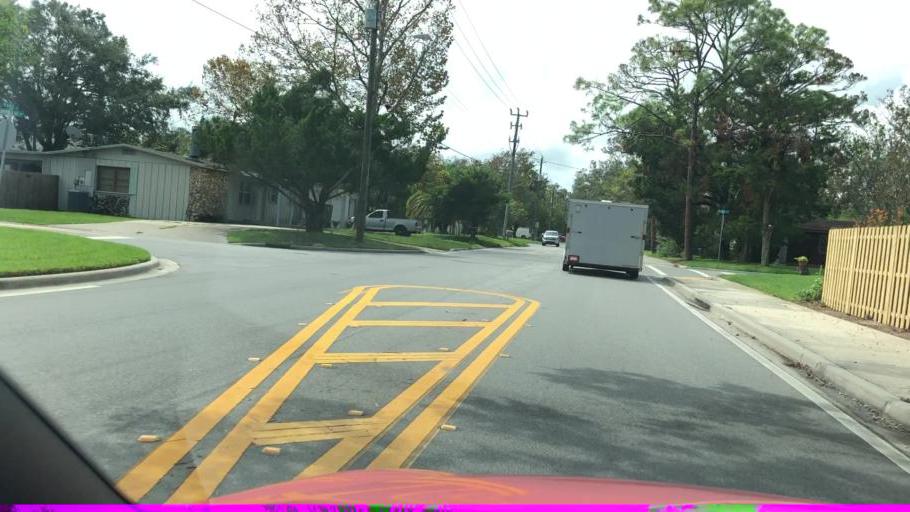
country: US
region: Florida
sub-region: Volusia County
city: Ormond Beach
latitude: 29.2693
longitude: -81.0625
